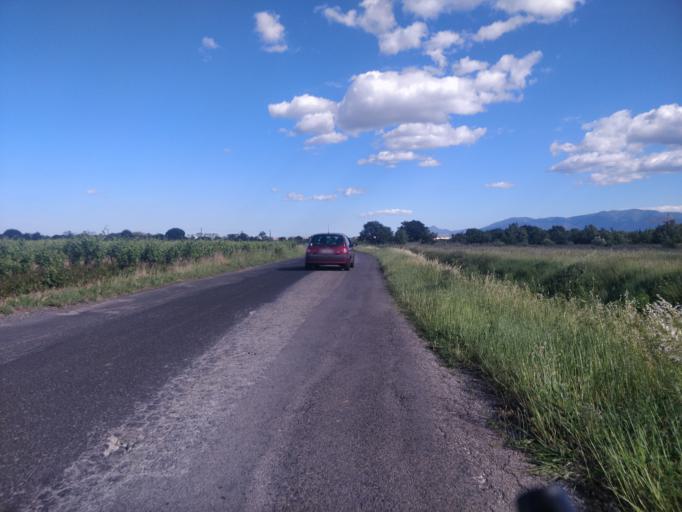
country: FR
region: Languedoc-Roussillon
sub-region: Departement des Pyrenees-Orientales
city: Cabestany
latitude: 42.6697
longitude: 2.9292
